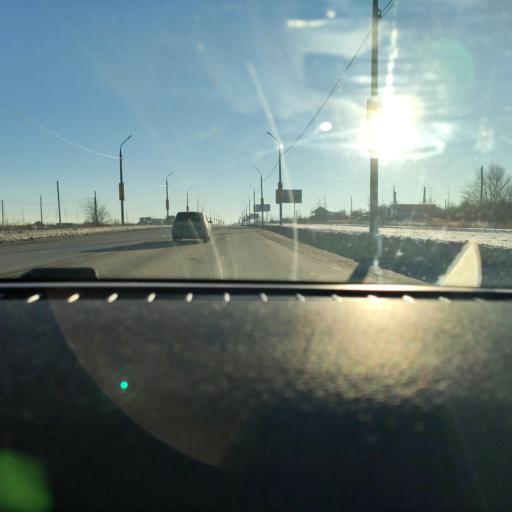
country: RU
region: Samara
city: Novokuybyshevsk
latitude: 53.0813
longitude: 49.9983
